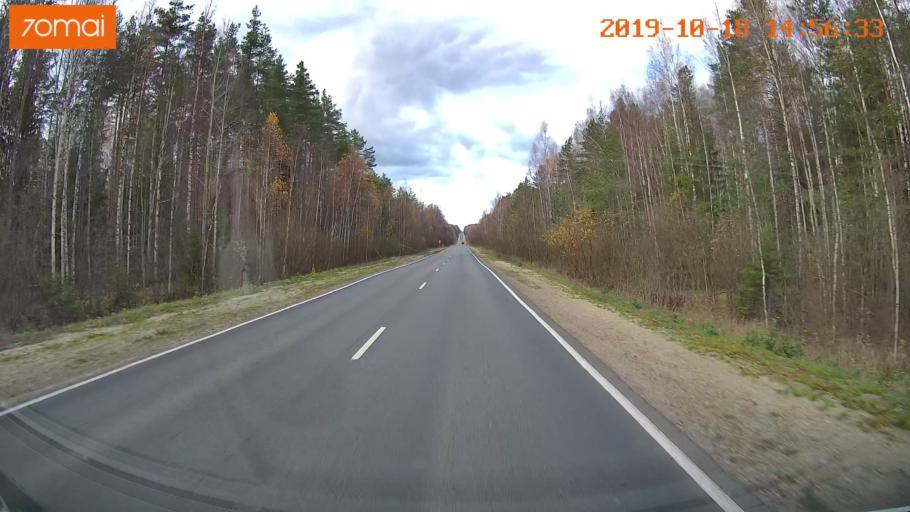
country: RU
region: Vladimir
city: Kurlovo
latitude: 55.4664
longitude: 40.5868
